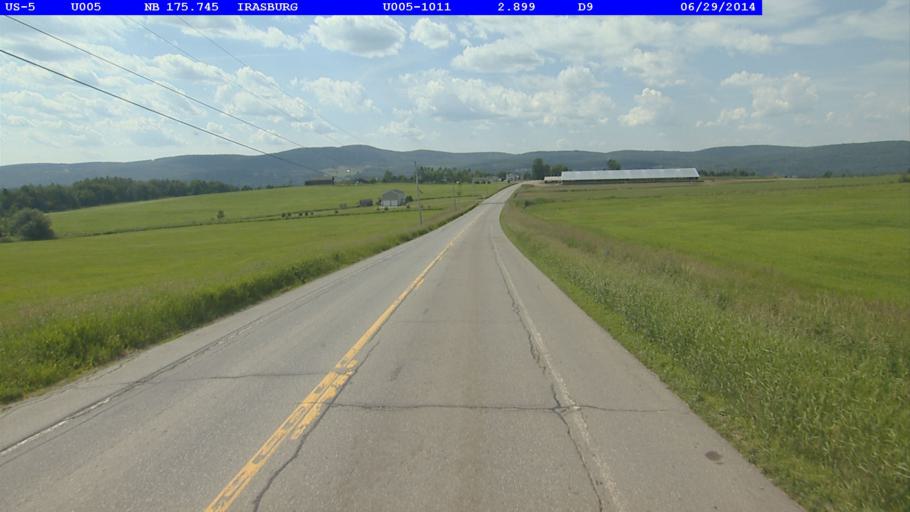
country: US
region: Vermont
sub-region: Orleans County
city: Newport
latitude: 44.8358
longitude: -72.2535
